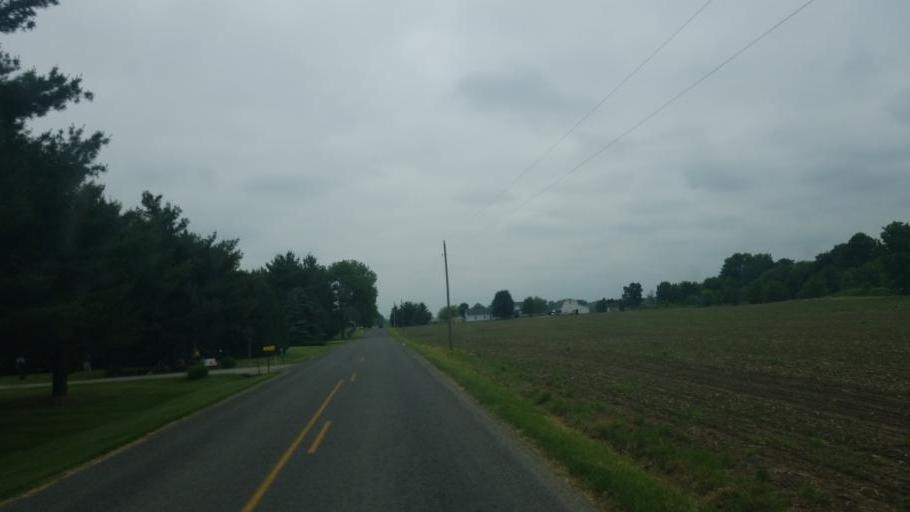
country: US
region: Indiana
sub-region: Elkhart County
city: Nappanee
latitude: 41.4709
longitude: -86.0498
